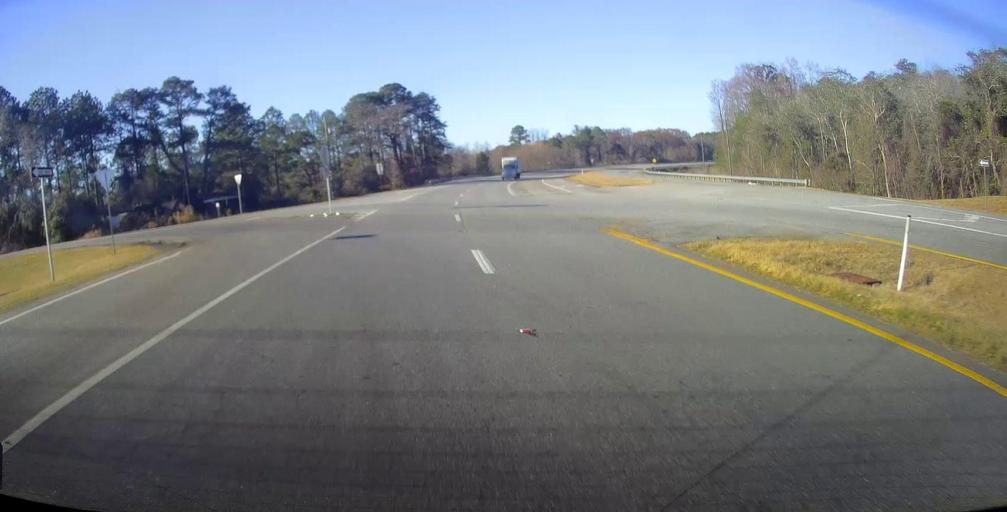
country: US
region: Georgia
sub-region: Sumter County
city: Americus
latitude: 31.9241
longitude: -84.2656
